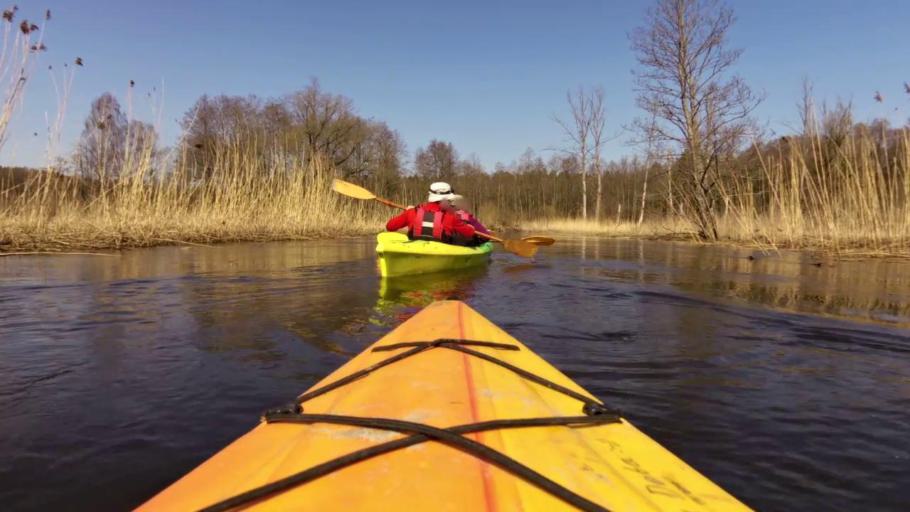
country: PL
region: West Pomeranian Voivodeship
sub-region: Powiat lobeski
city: Radowo Male
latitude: 53.7435
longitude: 15.5189
